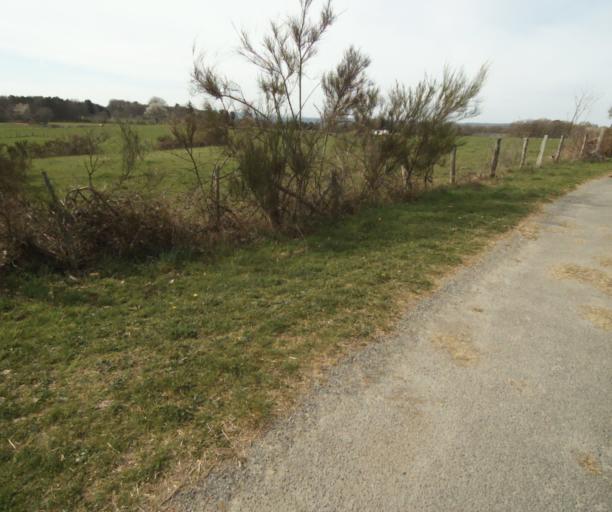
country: FR
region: Limousin
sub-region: Departement de la Correze
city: Correze
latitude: 45.4029
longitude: 1.8284
